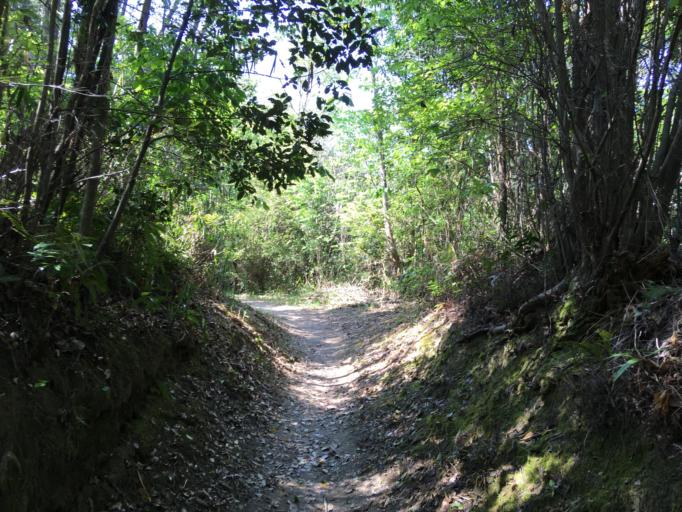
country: JP
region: Nara
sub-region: Ikoma-shi
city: Ikoma
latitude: 34.6967
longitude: 135.7165
